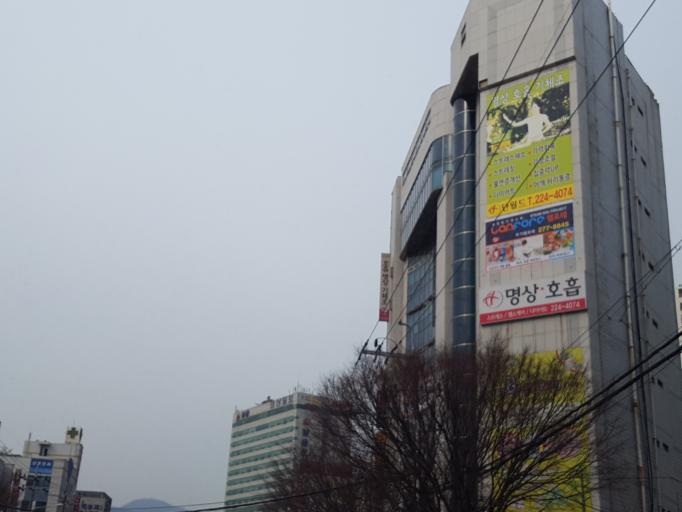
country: KR
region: Ulsan
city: Ulsan
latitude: 35.5524
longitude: 129.2685
